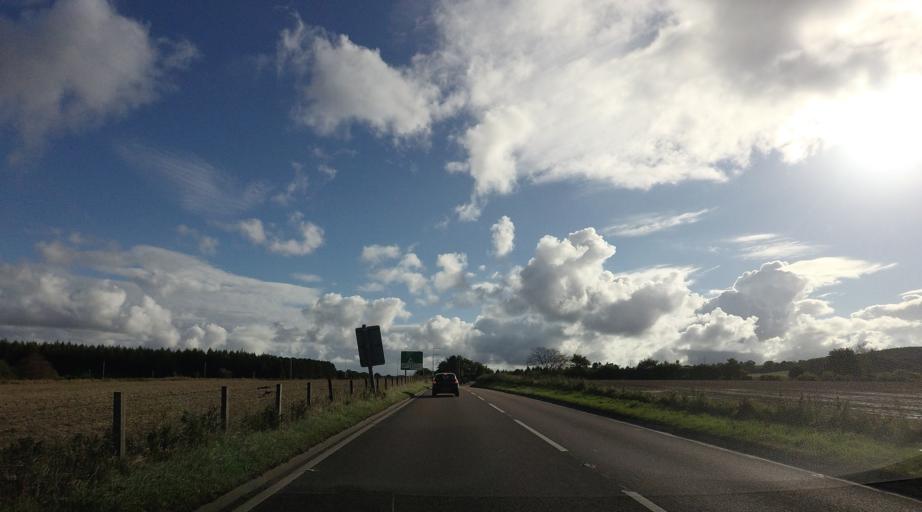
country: GB
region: Scotland
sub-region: Fife
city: Freuchie
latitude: 56.2357
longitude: -3.1553
